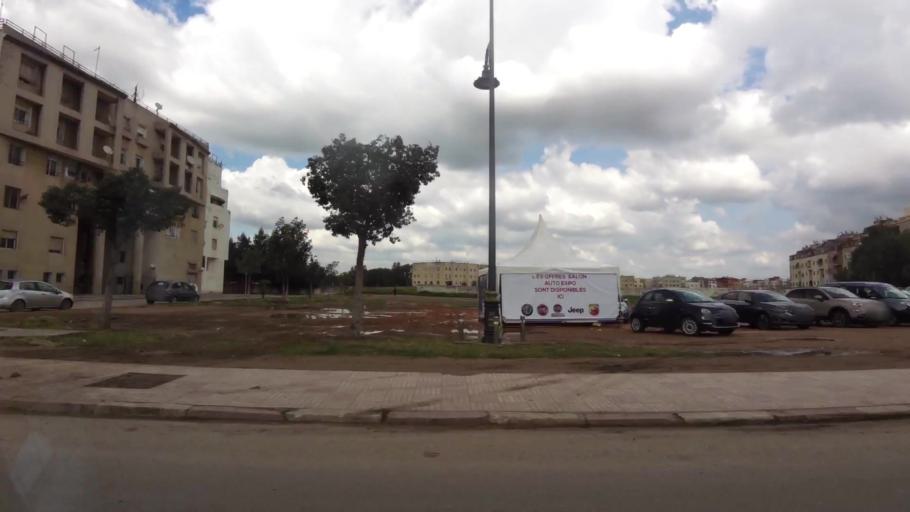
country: MA
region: Chaouia-Ouardigha
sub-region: Settat Province
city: Berrechid
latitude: 33.2688
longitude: -7.5841
